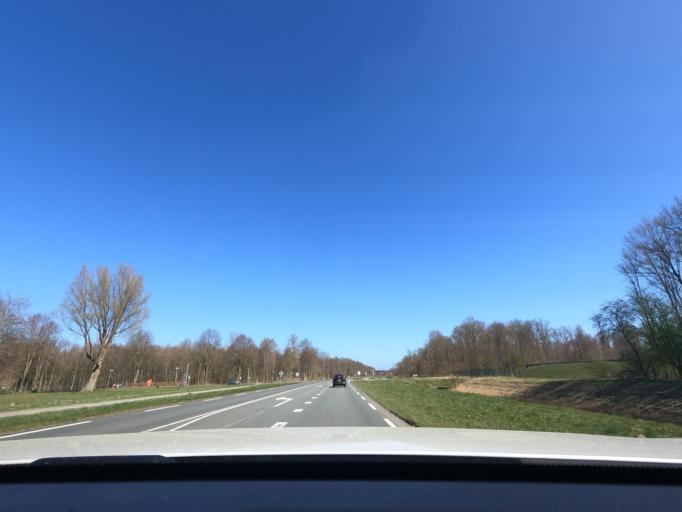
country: NL
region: Gelderland
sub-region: Gemeente Nunspeet
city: Nunspeet
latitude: 52.4393
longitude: 5.7721
